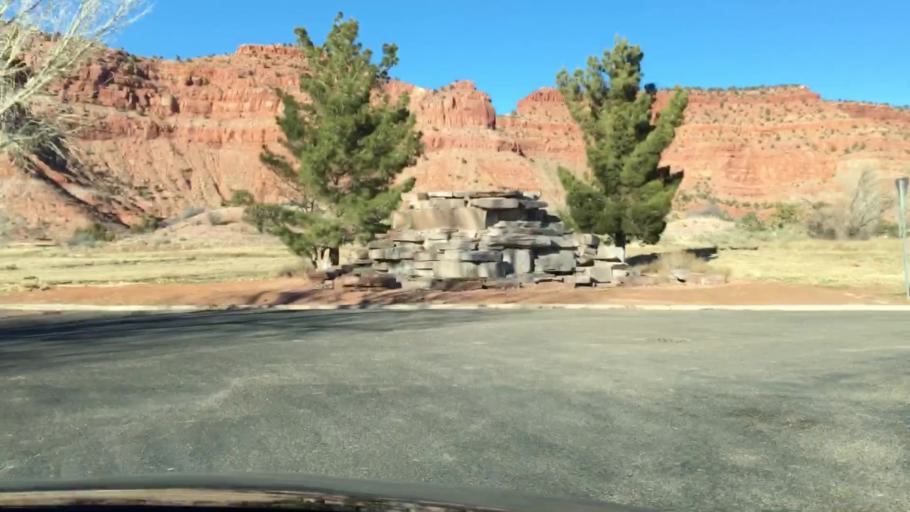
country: US
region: Utah
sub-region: Kane County
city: Kanab
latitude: 37.0432
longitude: -112.5130
